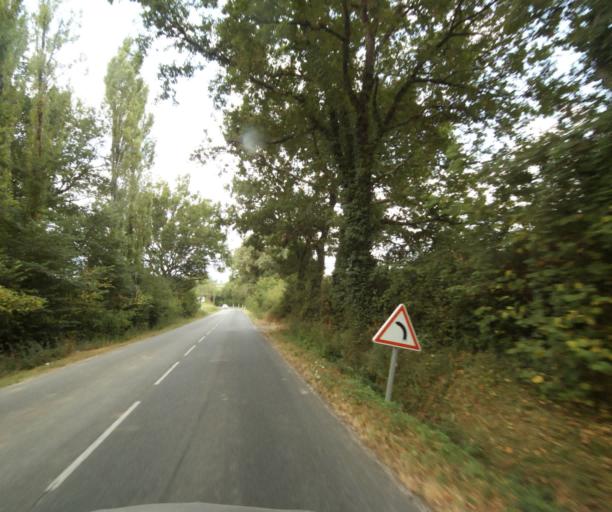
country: FR
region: Aquitaine
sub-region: Departement de la Gironde
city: Creon
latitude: 44.7644
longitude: -0.3613
